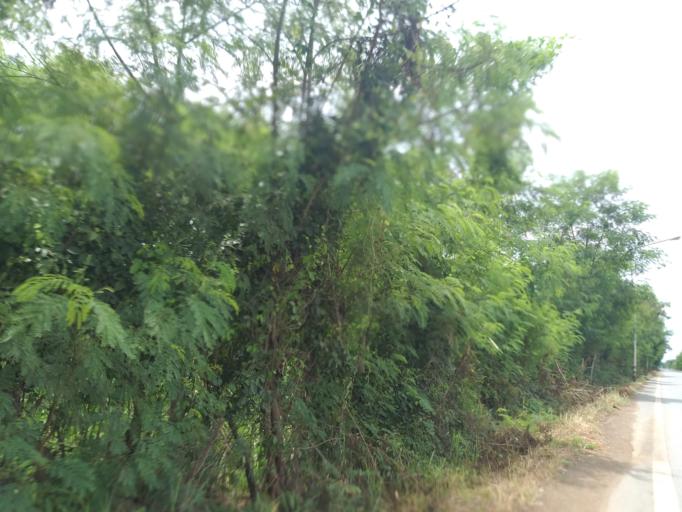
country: TH
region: Pathum Thani
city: Nong Suea
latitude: 14.0549
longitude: 100.8712
